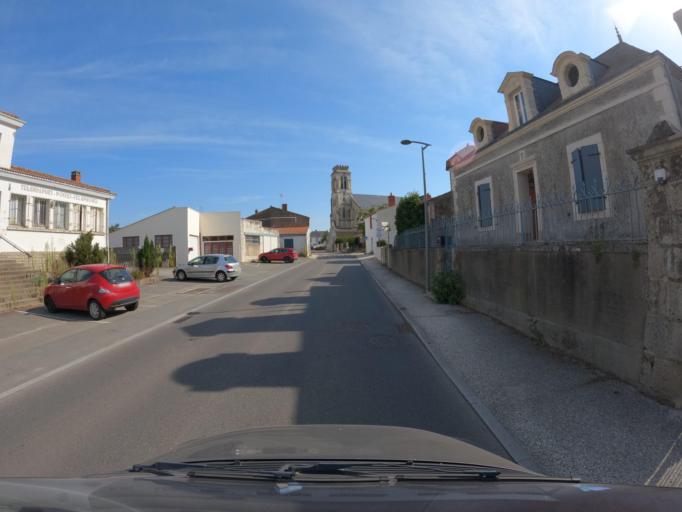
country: FR
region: Pays de la Loire
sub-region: Departement de la Vendee
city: Saint-Christophe-du-Ligneron
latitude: 46.8230
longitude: -1.7630
